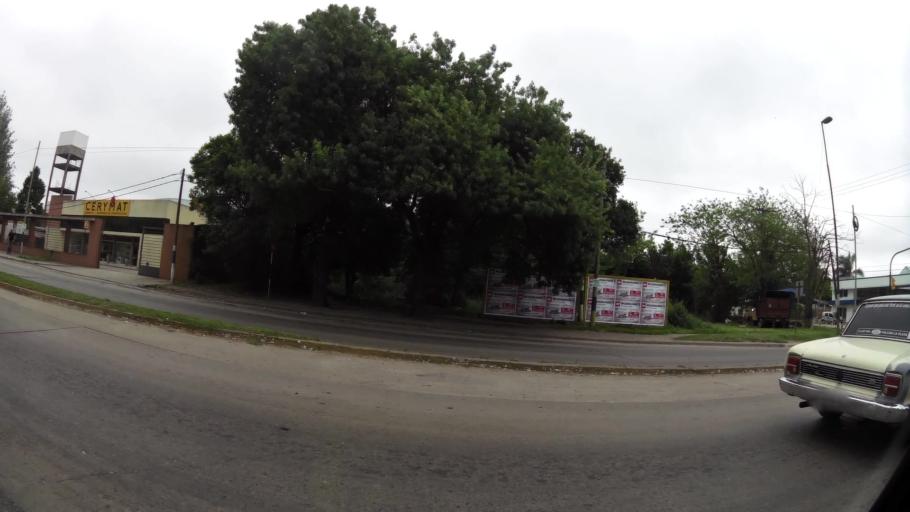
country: AR
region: Buenos Aires
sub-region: Partido de La Plata
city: La Plata
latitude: -34.9620
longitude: -58.0115
